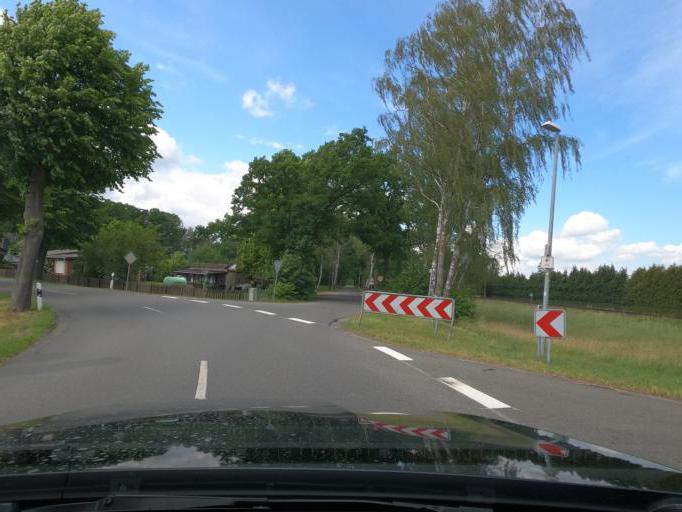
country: DE
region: Lower Saxony
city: Essel
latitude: 52.6335
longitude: 9.6428
